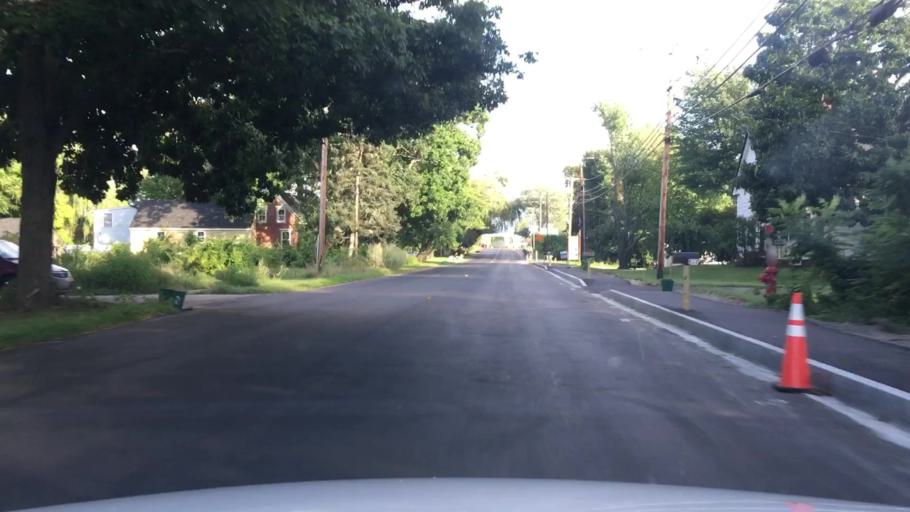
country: US
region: Maine
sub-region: York County
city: Eliot
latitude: 43.1234
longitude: -70.8337
